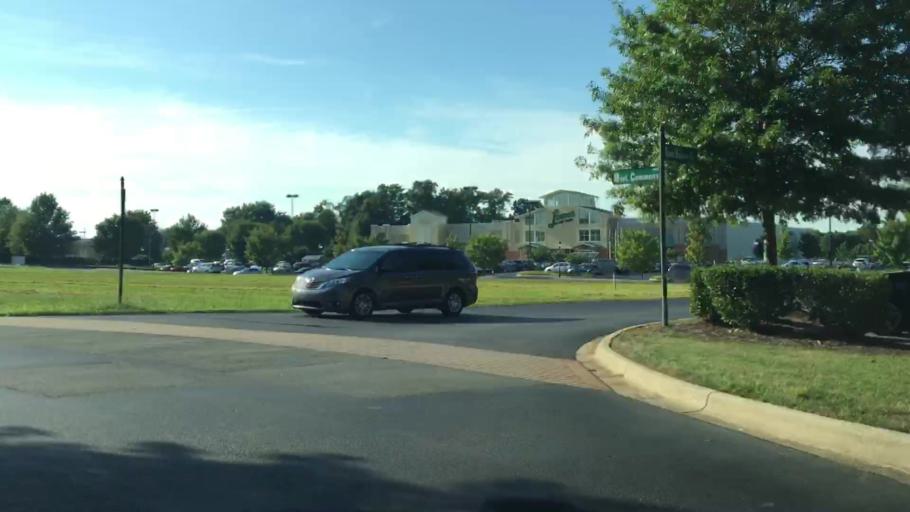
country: US
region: North Carolina
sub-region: Iredell County
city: Mooresville
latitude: 35.5862
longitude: -80.8710
